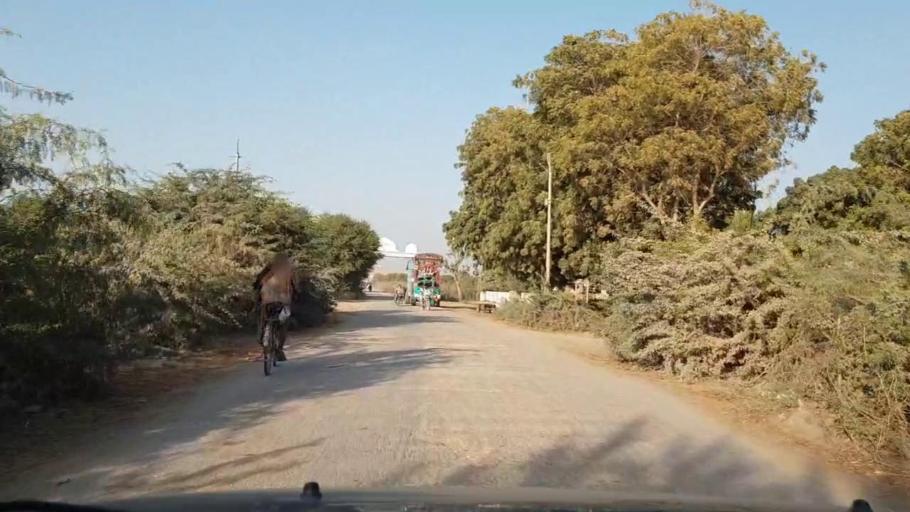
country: PK
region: Sindh
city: Chambar
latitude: 25.2832
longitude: 68.8102
